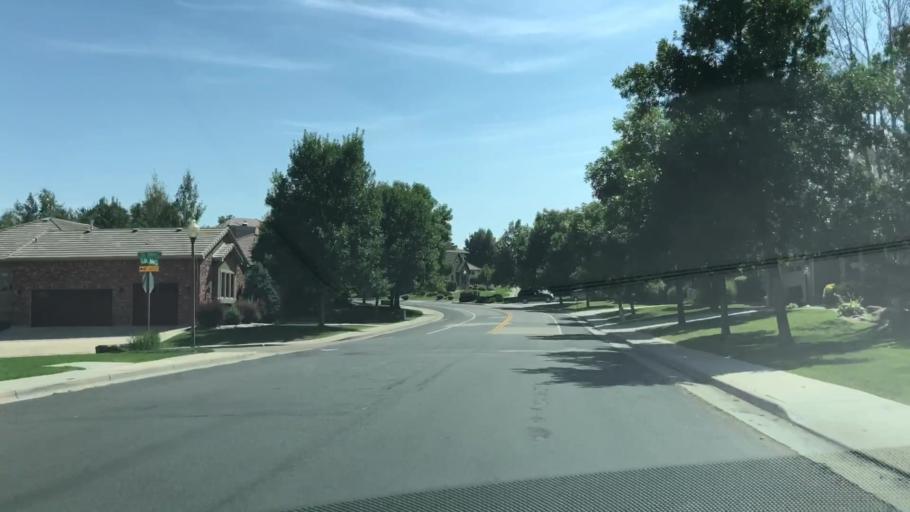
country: US
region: Colorado
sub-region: Larimer County
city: Loveland
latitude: 40.4011
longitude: -105.1509
